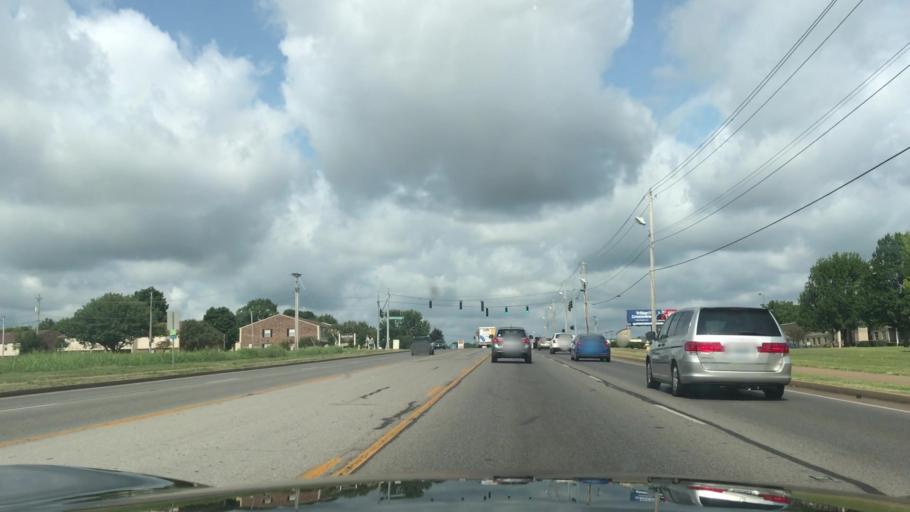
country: US
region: Kentucky
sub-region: Warren County
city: Bowling Green
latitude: 36.9610
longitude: -86.4577
